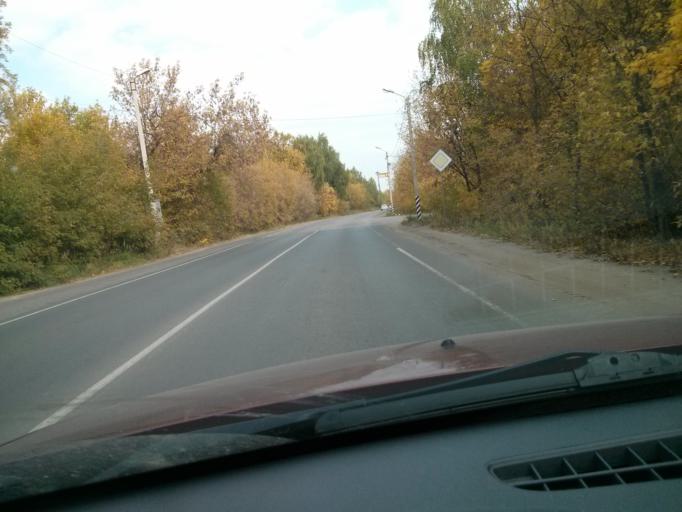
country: RU
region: Vladimir
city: Murom
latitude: 55.5607
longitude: 42.0240
